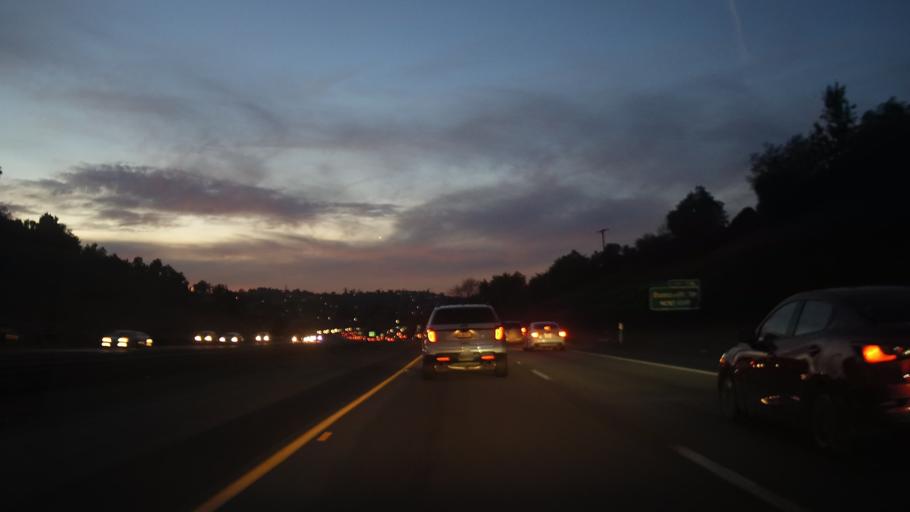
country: US
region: California
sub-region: San Diego County
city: Spring Valley
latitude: 32.7493
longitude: -116.9956
